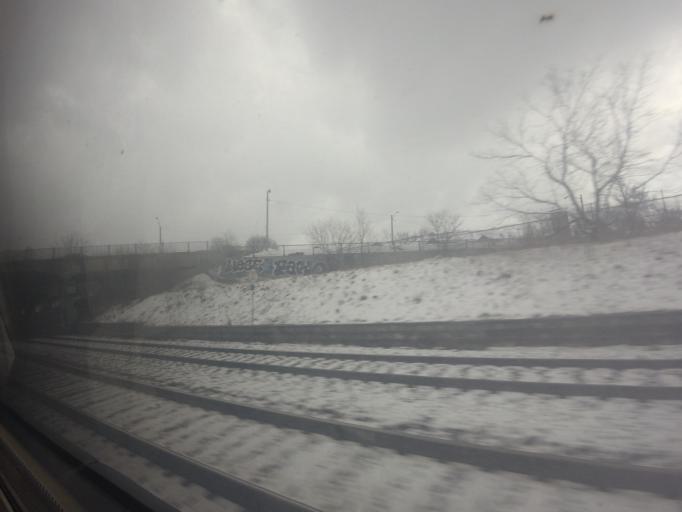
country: CA
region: Ontario
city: Scarborough
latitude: 43.7002
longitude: -79.2660
